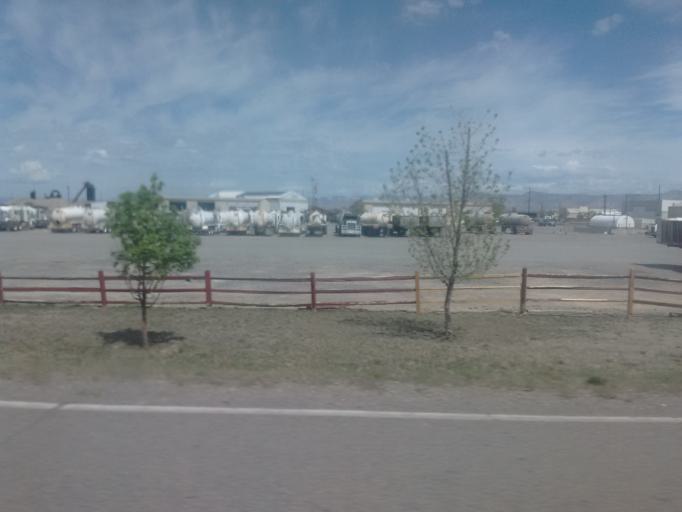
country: US
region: Colorado
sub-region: Mesa County
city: Redlands
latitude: 39.0902
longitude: -108.6138
